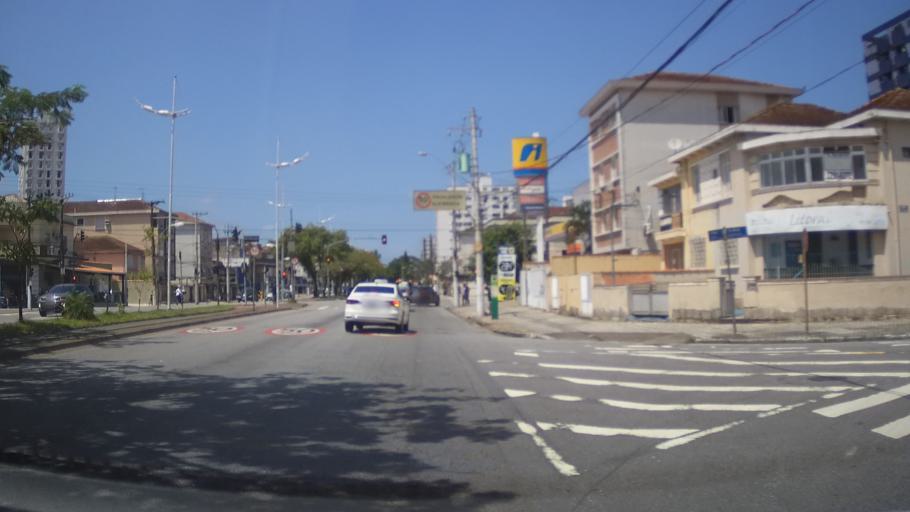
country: BR
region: Sao Paulo
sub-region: Santos
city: Santos
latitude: -23.9627
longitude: -46.3146
